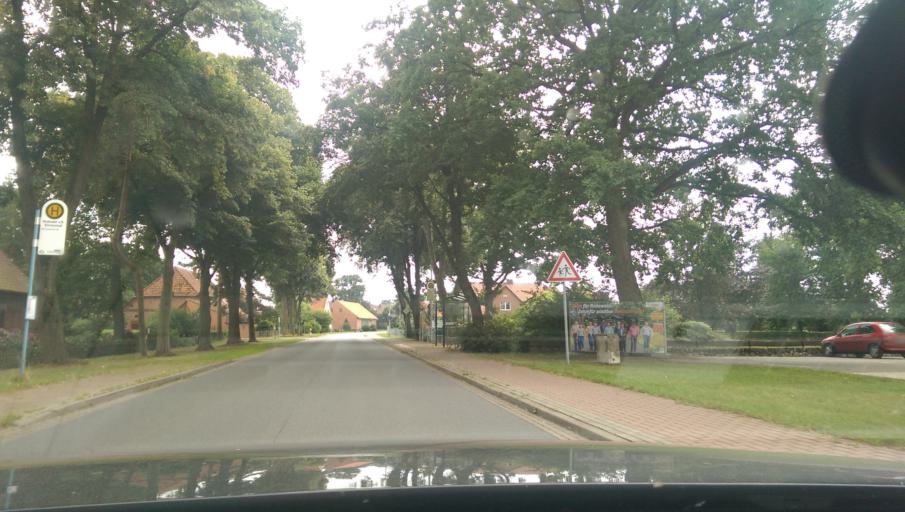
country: DE
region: Lower Saxony
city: Frankenfeld
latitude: 52.6941
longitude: 9.4810
